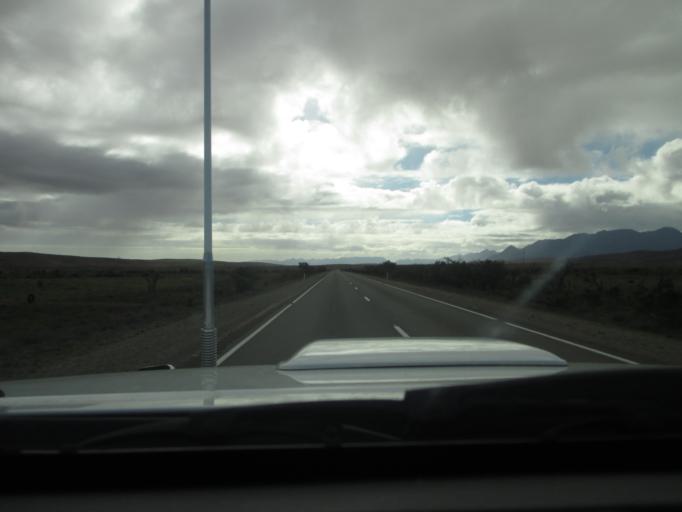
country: AU
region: South Australia
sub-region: Flinders Ranges
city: Quorn
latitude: -31.6111
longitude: 138.3978
